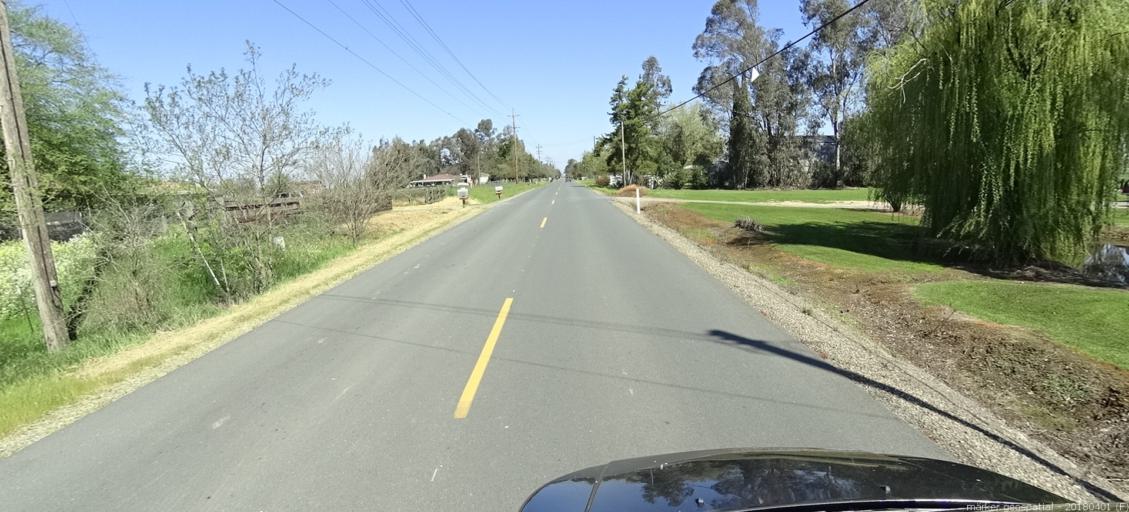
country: US
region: California
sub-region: Sacramento County
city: Herald
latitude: 38.3392
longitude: -121.2421
